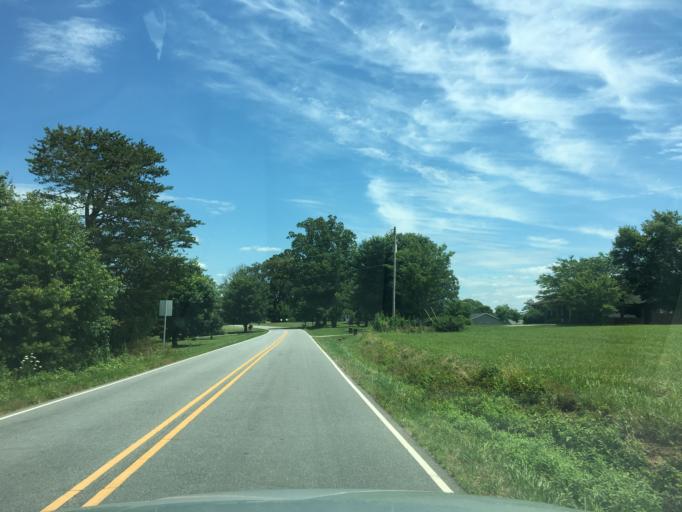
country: US
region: North Carolina
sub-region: Burke County
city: Glen Alpine
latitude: 35.6457
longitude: -81.7897
